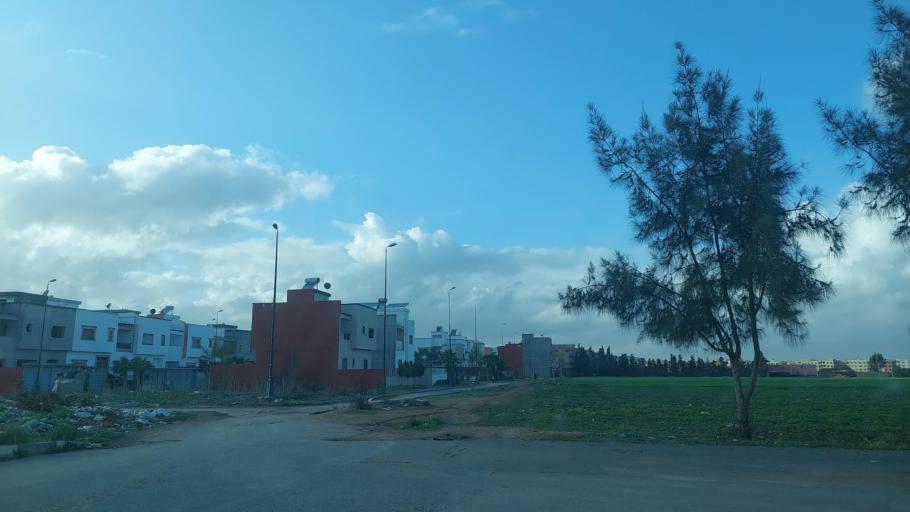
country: MA
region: Grand Casablanca
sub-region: Mediouna
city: Mediouna
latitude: 33.3763
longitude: -7.5273
